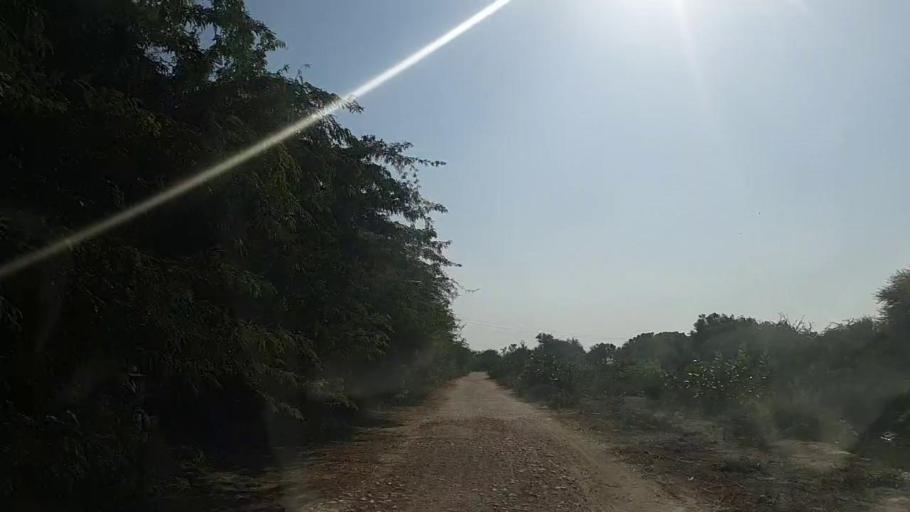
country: PK
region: Sindh
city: Mirpur Batoro
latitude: 24.6298
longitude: 68.1610
